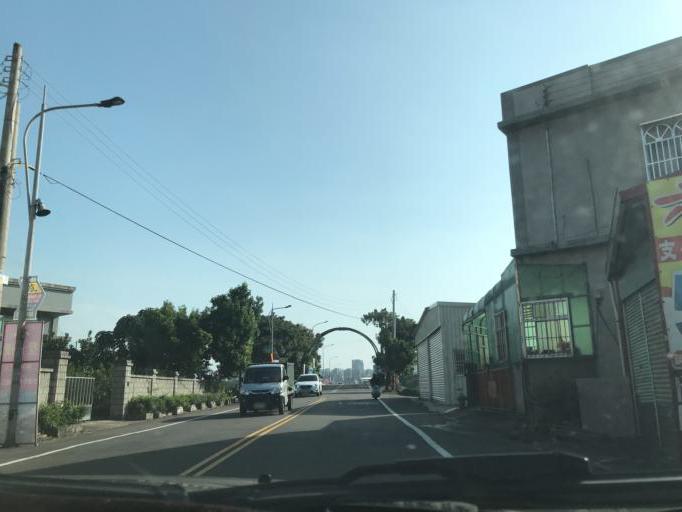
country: TW
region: Taiwan
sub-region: Hsinchu
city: Zhubei
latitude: 24.8397
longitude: 121.0364
